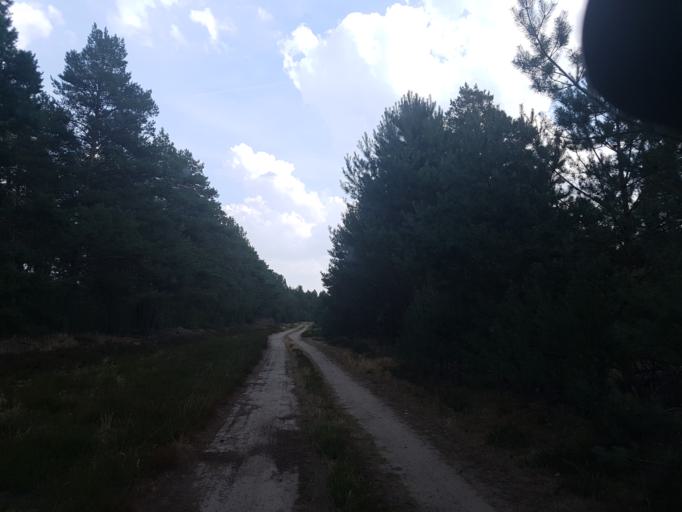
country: DE
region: Brandenburg
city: Treuenbrietzen
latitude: 52.0536
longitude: 12.8413
